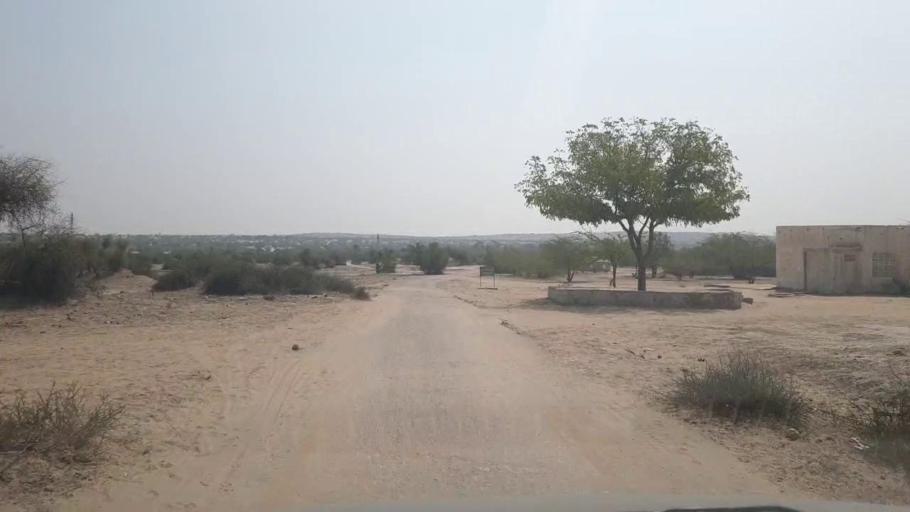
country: PK
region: Sindh
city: Chor
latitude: 25.4568
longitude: 69.7889
